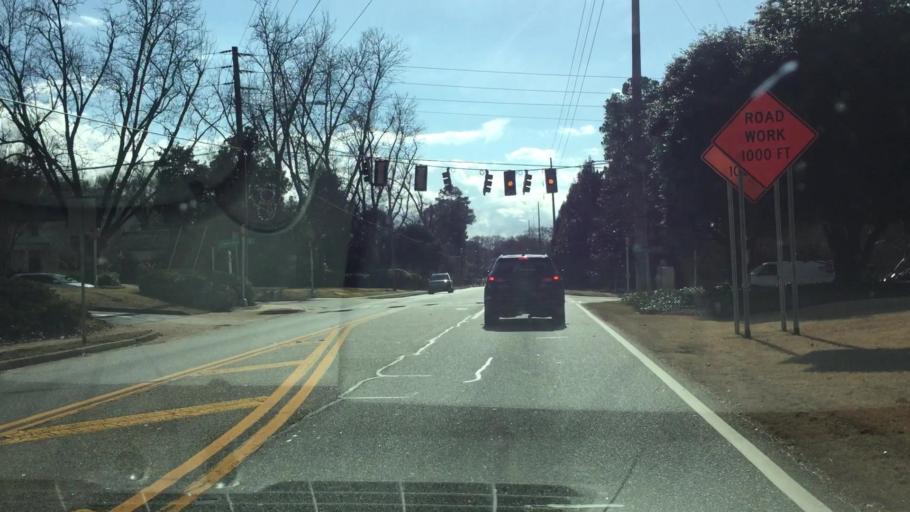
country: US
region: Georgia
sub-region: Henry County
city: McDonough
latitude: 33.4519
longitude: -84.1416
